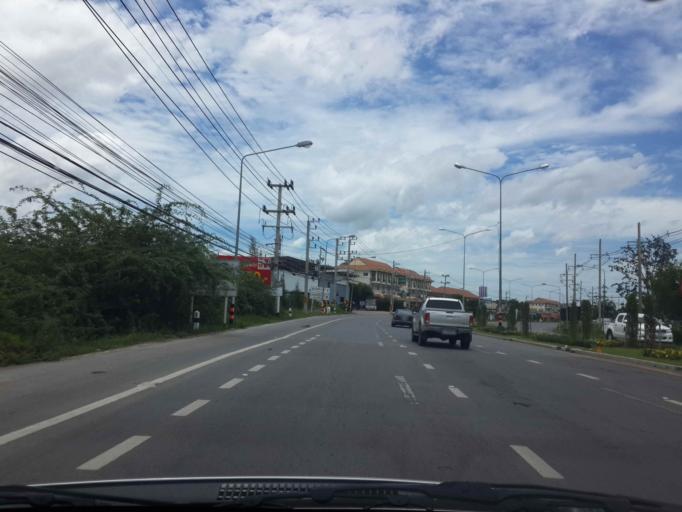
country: TH
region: Prachuap Khiri Khan
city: Hua Hin
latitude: 12.6344
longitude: 99.9488
